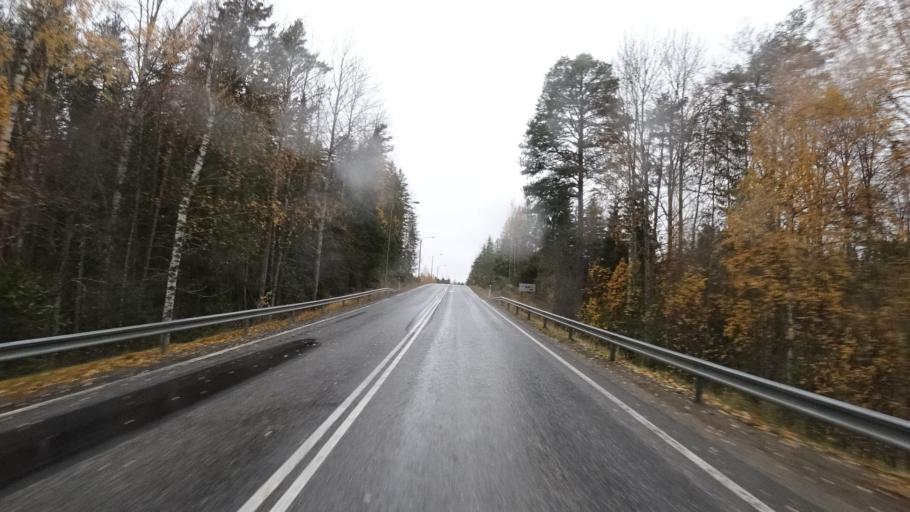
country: FI
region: Northern Savo
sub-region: Koillis-Savo
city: Tuusniemi
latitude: 62.7970
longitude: 28.5355
